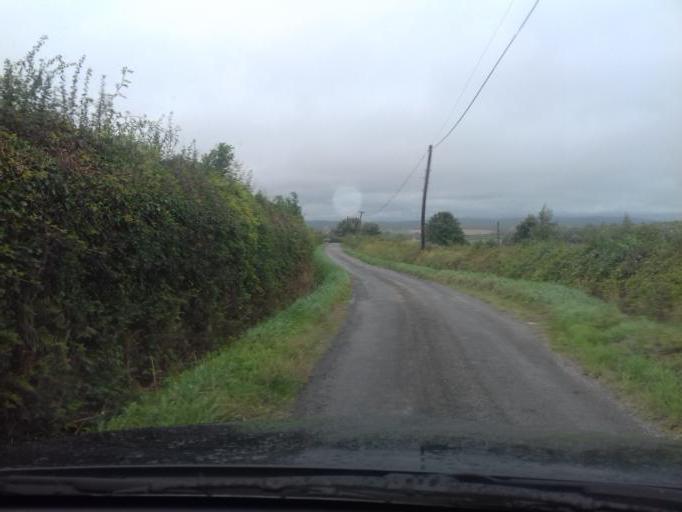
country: IE
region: Leinster
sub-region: Kilkenny
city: Graiguenamanagh
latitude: 52.5957
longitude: -7.0100
